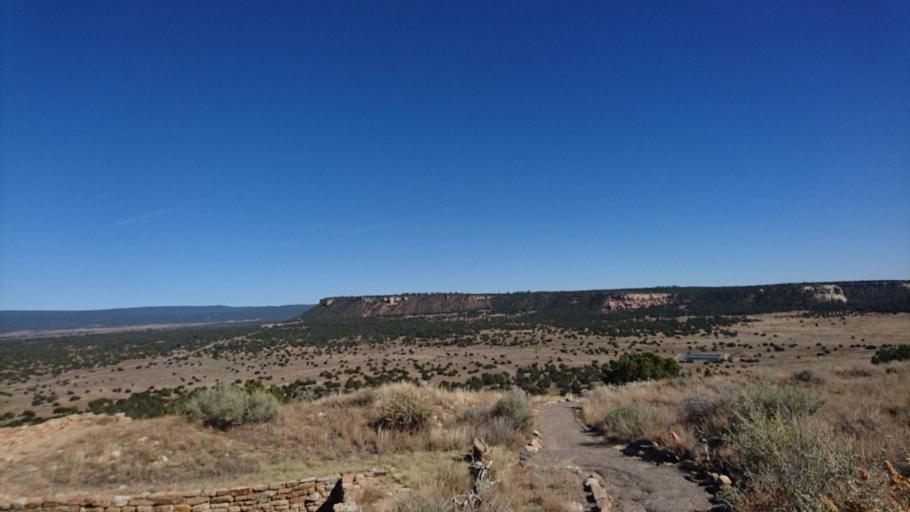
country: US
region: New Mexico
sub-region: McKinley County
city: Thoreau
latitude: 35.0380
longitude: -108.3536
